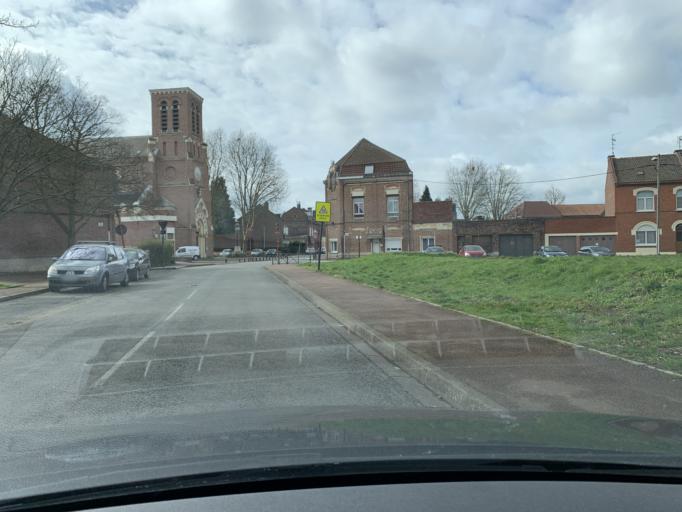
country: FR
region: Nord-Pas-de-Calais
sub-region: Departement du Nord
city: Flers-en-Escrebieux
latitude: 50.3945
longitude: 3.0852
